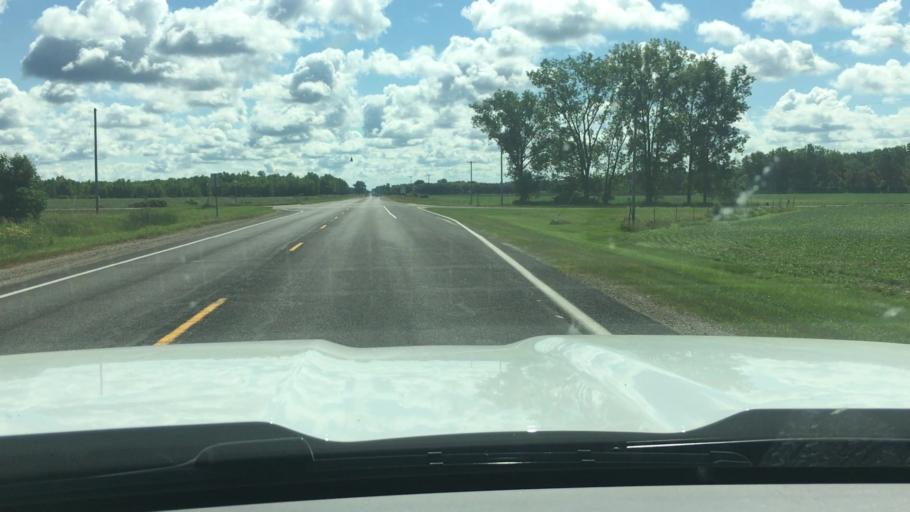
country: US
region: Michigan
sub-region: Clinton County
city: Ovid
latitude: 43.1759
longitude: -84.4492
